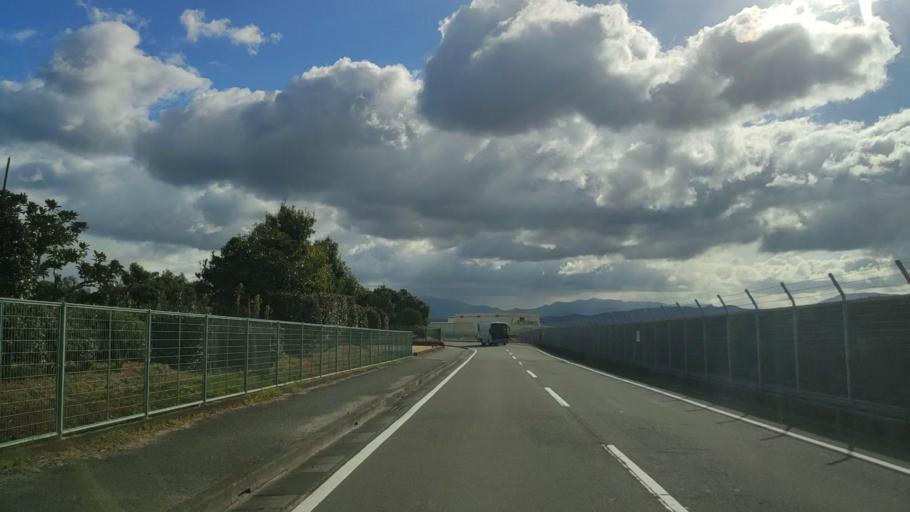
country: JP
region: Ehime
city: Masaki-cho
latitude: 33.8229
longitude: 132.7100
